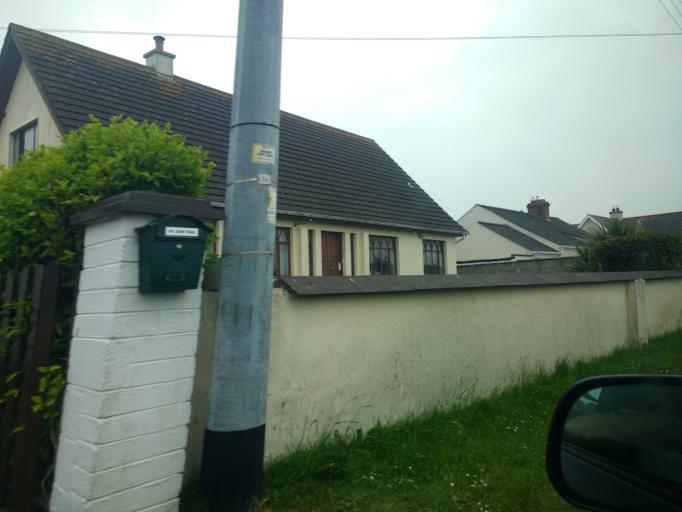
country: IE
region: Leinster
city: Portraine
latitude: 53.4755
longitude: -6.1225
